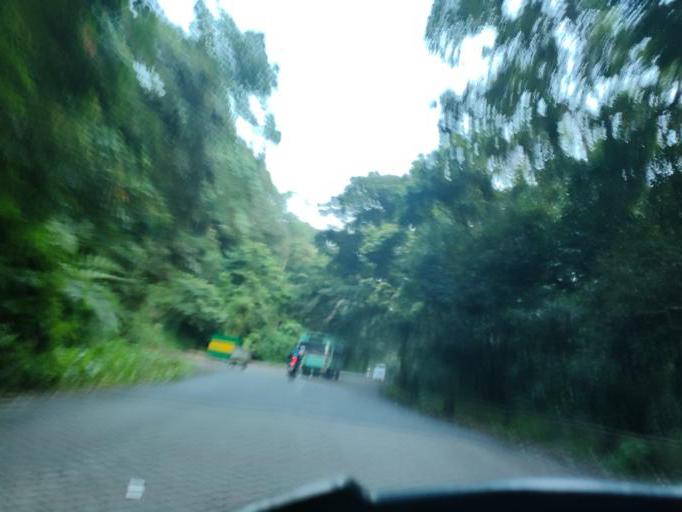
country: IN
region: Tamil Nadu
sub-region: Dindigul
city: Kodaikanal
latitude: 10.2491
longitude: 77.5203
